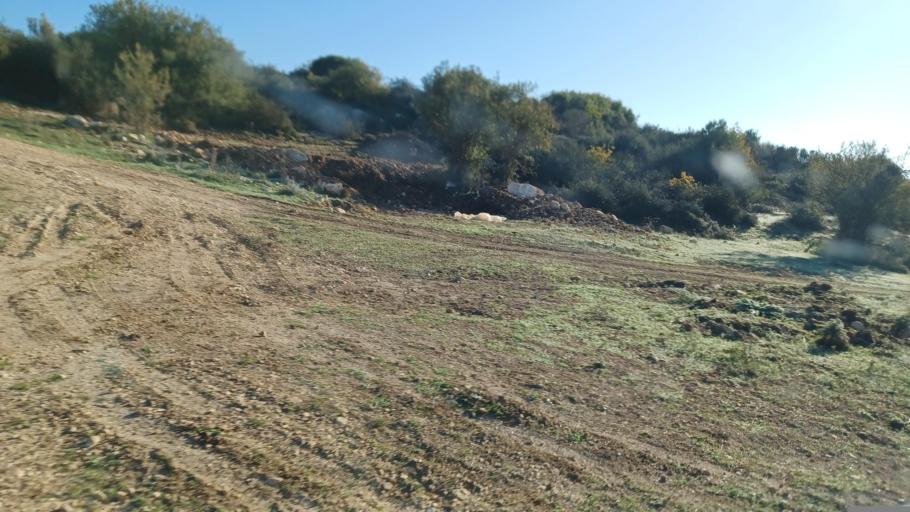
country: CY
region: Pafos
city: Polis
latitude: 34.9788
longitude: 32.5171
